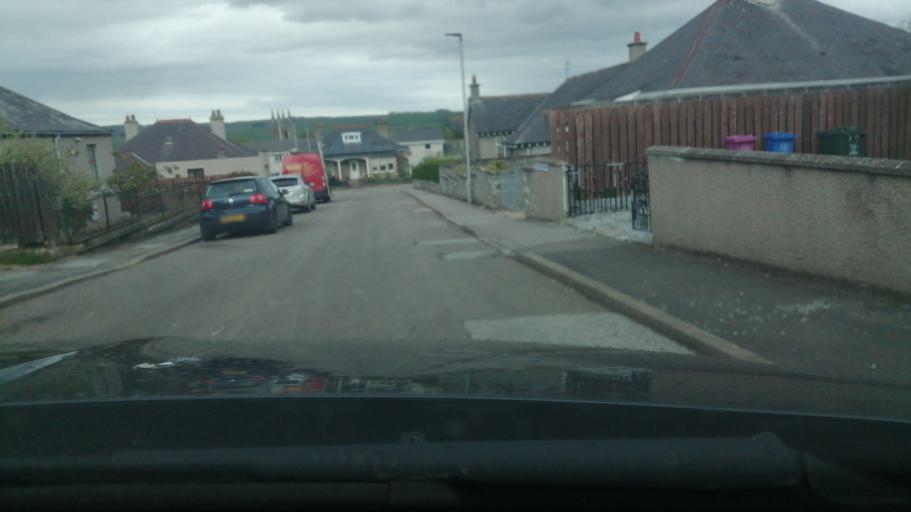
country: GB
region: Scotland
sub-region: Moray
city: Keith
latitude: 57.5411
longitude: -2.9541
